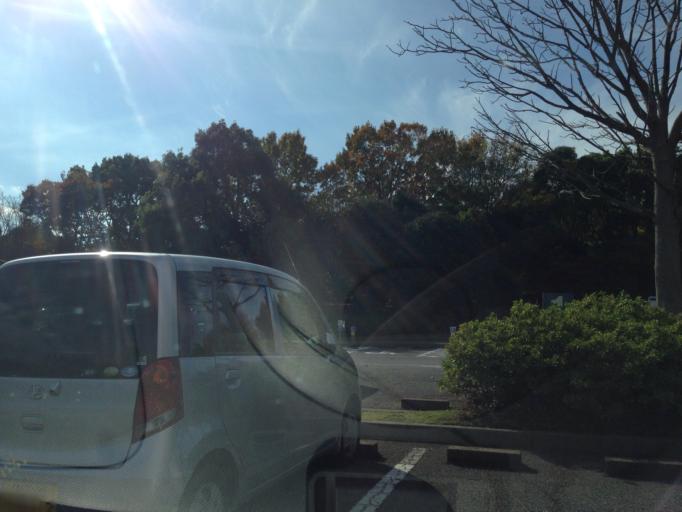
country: JP
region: Chiba
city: Kashiwa
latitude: 35.8942
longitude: 139.9418
